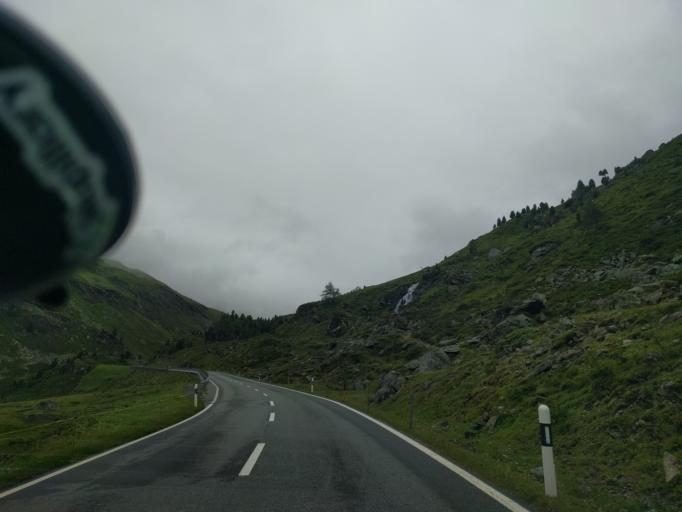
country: CH
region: Grisons
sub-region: Praettigau/Davos District
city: Davos
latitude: 46.7818
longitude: 9.9228
